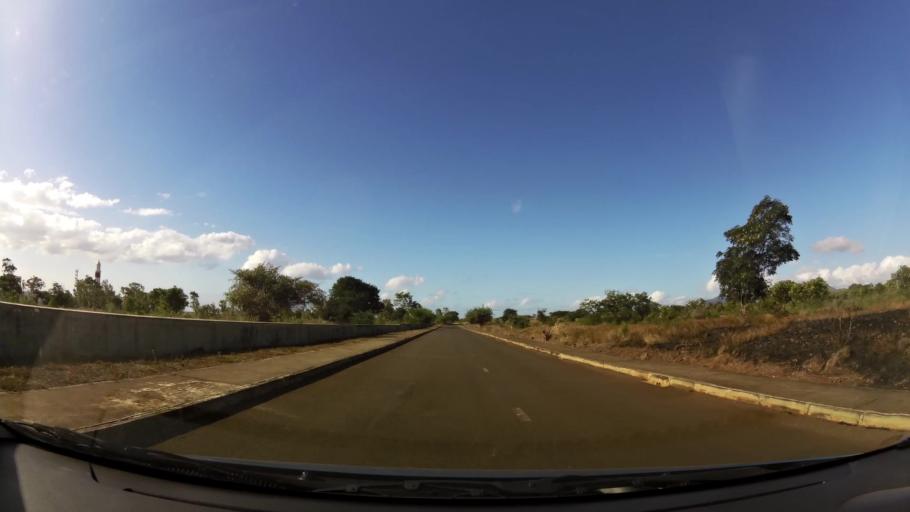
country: MU
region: Black River
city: Albion
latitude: -20.1944
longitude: 57.4113
